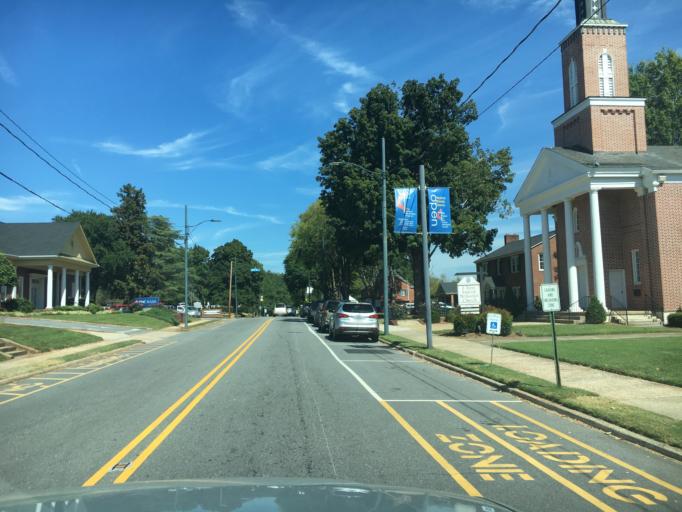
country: US
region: North Carolina
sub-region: Rutherford County
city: Rutherfordton
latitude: 35.3697
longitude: -81.9567
